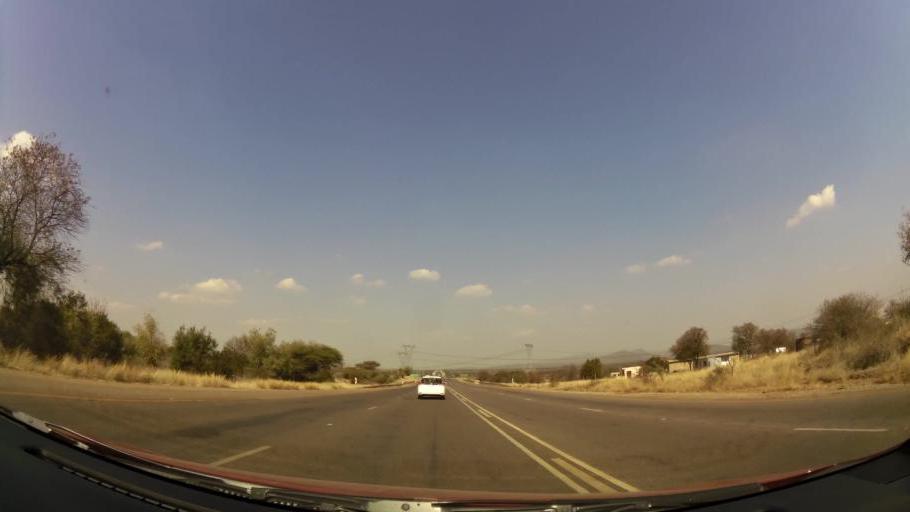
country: ZA
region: North-West
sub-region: Bojanala Platinum District Municipality
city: Mogwase
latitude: -25.3865
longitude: 27.0689
